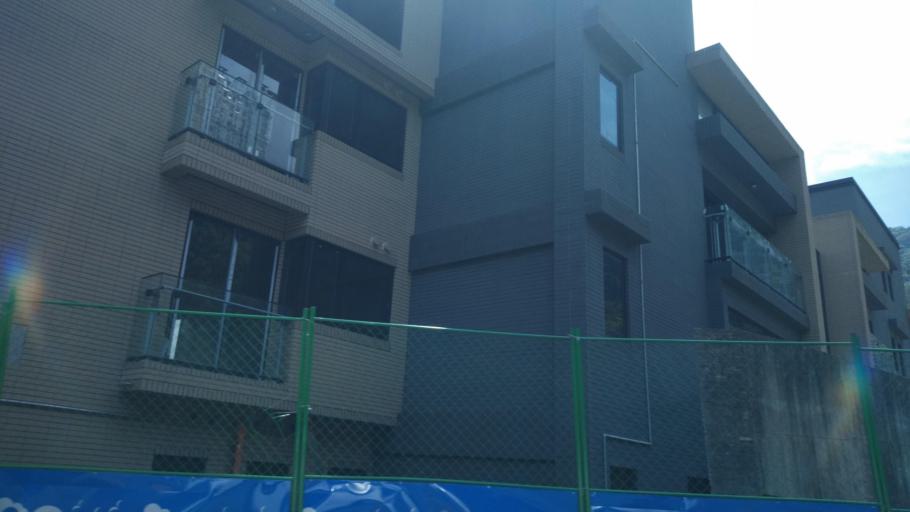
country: TW
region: Taipei
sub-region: Taipei
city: Banqiao
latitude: 24.9402
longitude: 121.5035
